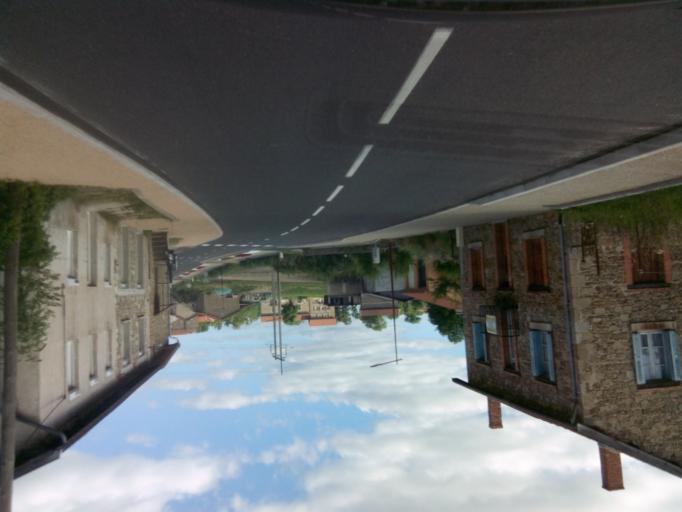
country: FR
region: Auvergne
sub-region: Departement de la Haute-Loire
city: Saint-Paulien
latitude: 45.2181
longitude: 3.8178
